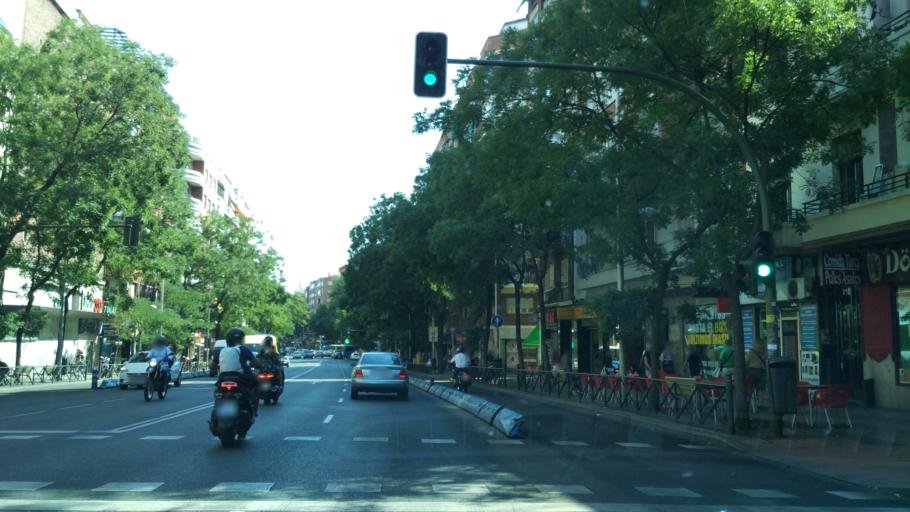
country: ES
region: Madrid
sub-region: Provincia de Madrid
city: Tetuan de las Victorias
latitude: 40.4566
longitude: -3.7021
